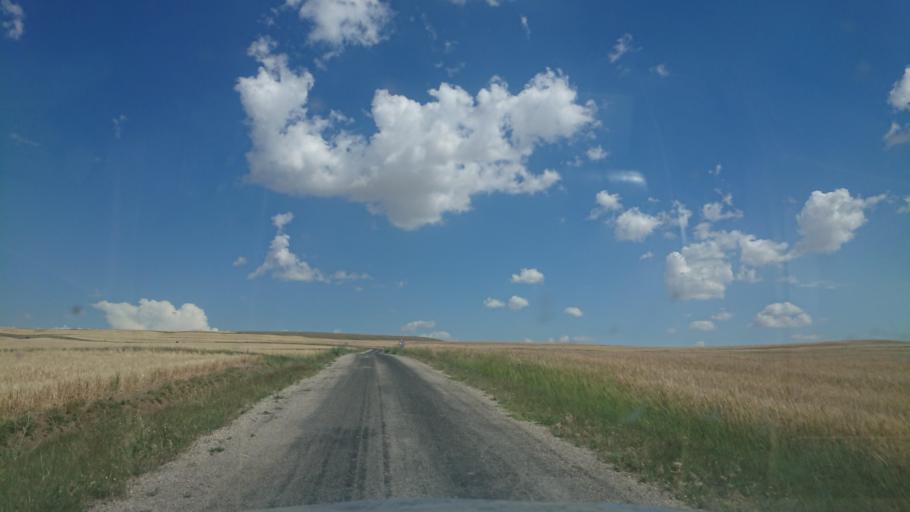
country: TR
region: Aksaray
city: Agacoren
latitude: 38.8076
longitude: 33.8001
